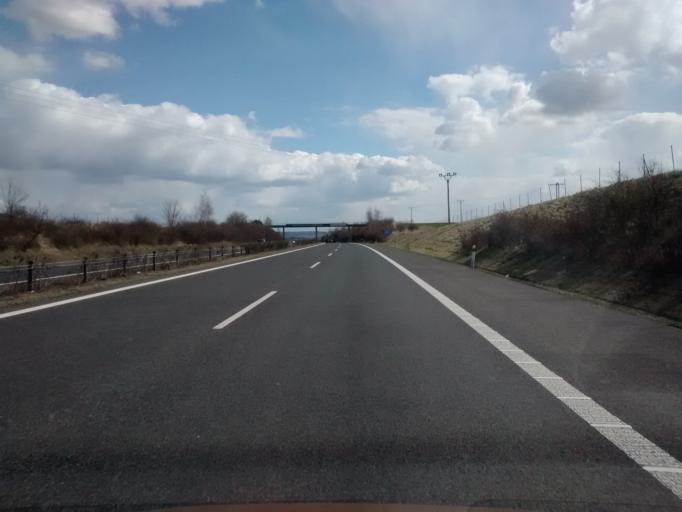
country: CZ
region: Central Bohemia
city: Nelahozeves
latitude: 50.3310
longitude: 14.2901
